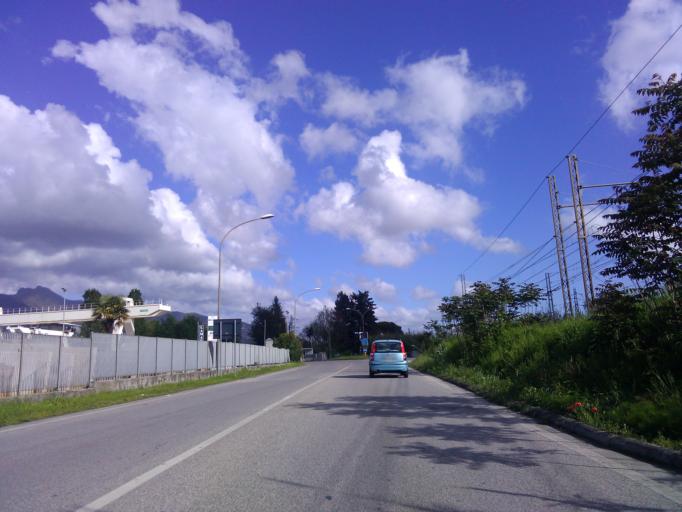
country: IT
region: Tuscany
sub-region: Provincia di Lucca
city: Strettoia
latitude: 43.9904
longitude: 10.1822
